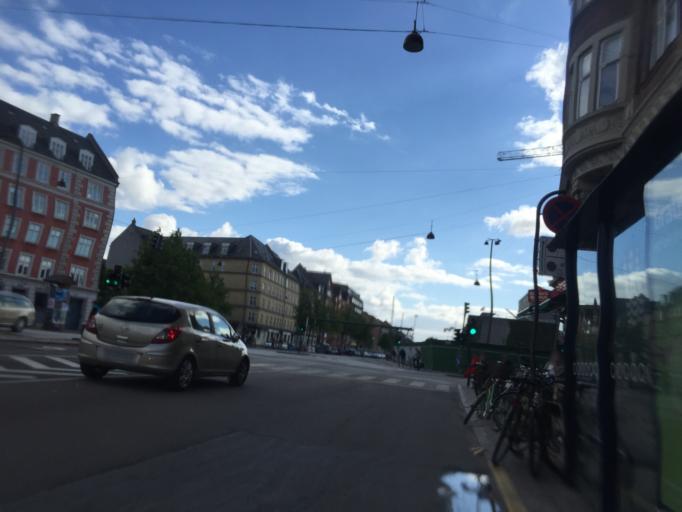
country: DK
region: Capital Region
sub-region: Kobenhavn
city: Copenhagen
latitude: 55.6995
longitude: 12.5770
